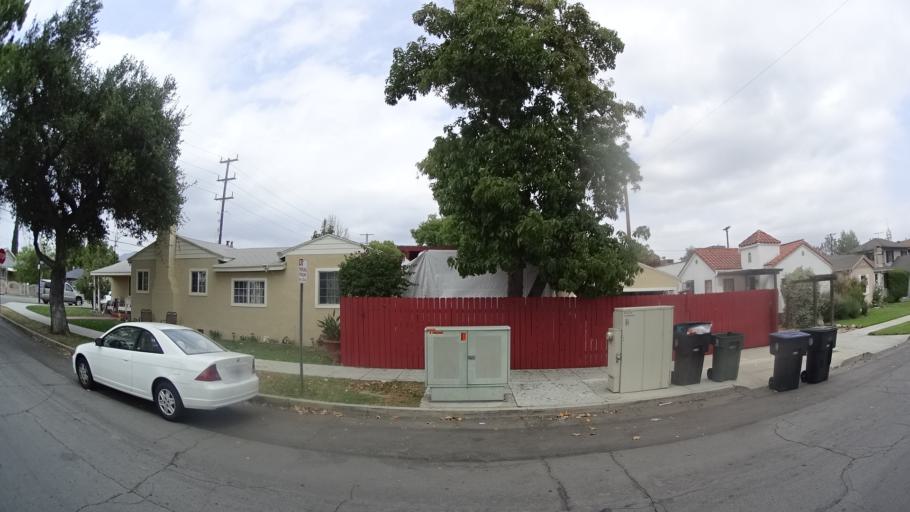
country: US
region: California
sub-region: Los Angeles County
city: Burbank
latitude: 34.1657
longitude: -118.3283
